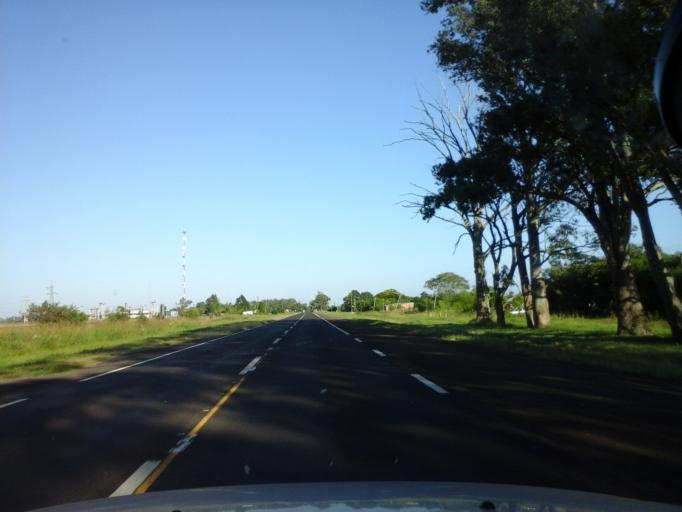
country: AR
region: Corrientes
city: Ita Ibate
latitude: -27.4484
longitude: -57.3323
